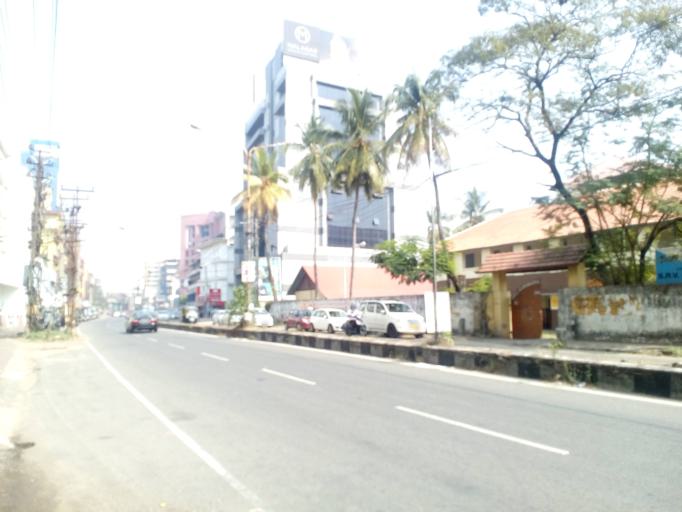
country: IN
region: Kerala
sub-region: Ernakulam
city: Cochin
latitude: 9.9704
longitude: 76.2858
